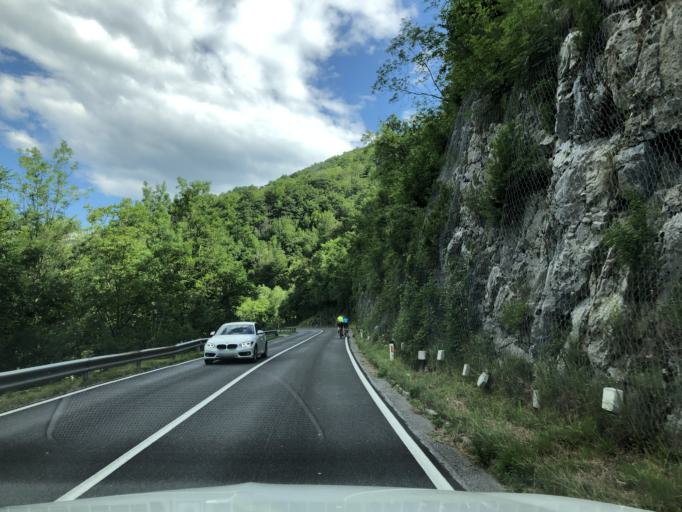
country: SI
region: Kanal
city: Deskle
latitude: 46.0357
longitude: 13.5983
